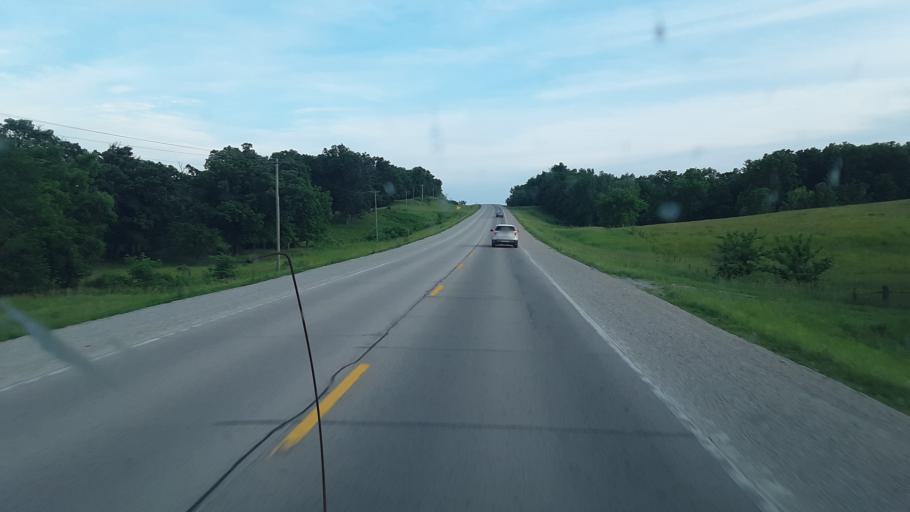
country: US
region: Iowa
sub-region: Benton County
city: Belle Plaine
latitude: 41.8407
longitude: -92.2787
